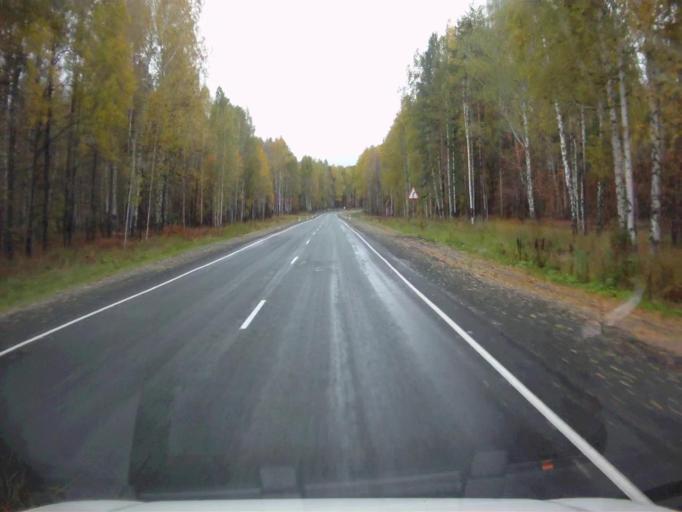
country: RU
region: Chelyabinsk
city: Nyazepetrovsk
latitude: 56.0623
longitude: 59.7274
